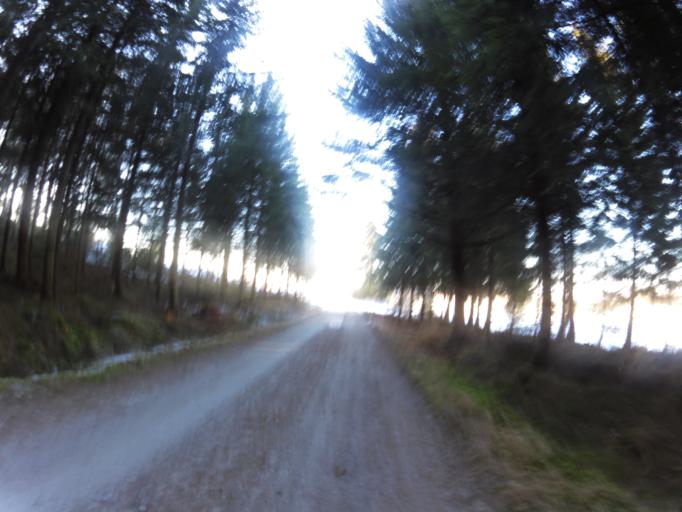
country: NO
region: Ostfold
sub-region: Fredrikstad
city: Lervik
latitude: 59.2427
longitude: 10.8165
